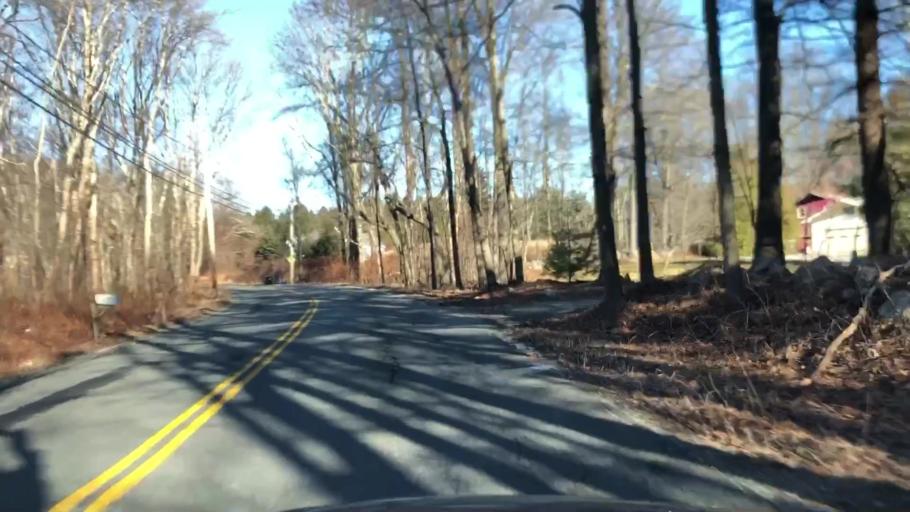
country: US
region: Massachusetts
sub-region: Worcester County
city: Charlton
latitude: 42.1109
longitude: -71.9710
